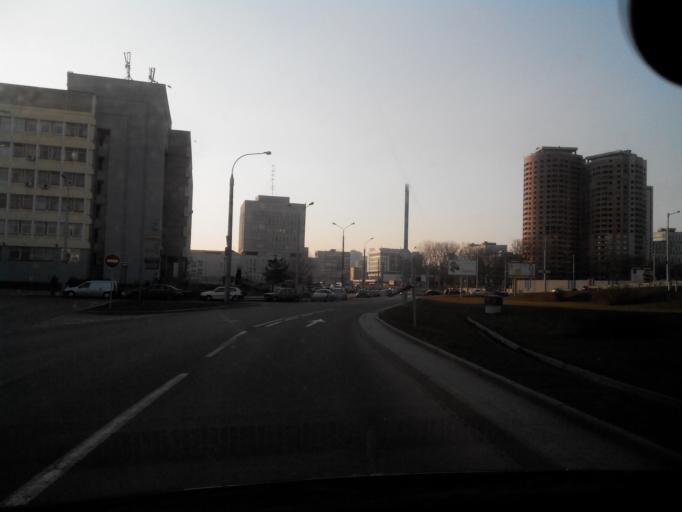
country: BY
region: Minsk
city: Minsk
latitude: 53.9063
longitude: 27.5224
